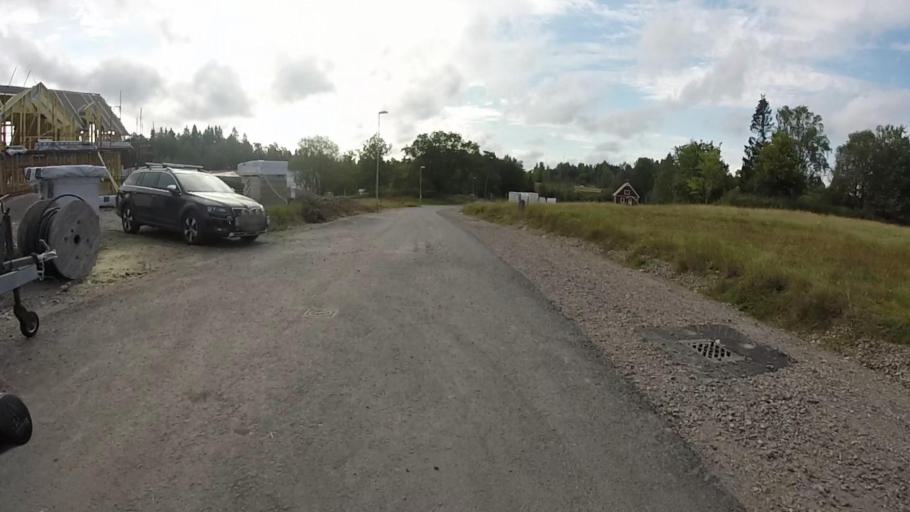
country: SE
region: Vaestra Goetaland
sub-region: Trollhattan
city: Trollhattan
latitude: 58.2765
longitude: 12.2494
